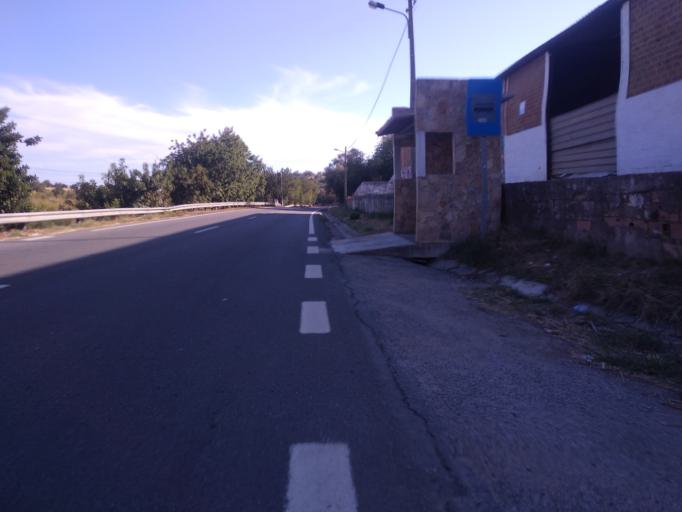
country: PT
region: Faro
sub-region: Sao Bras de Alportel
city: Sao Bras de Alportel
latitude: 37.1126
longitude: -7.9082
